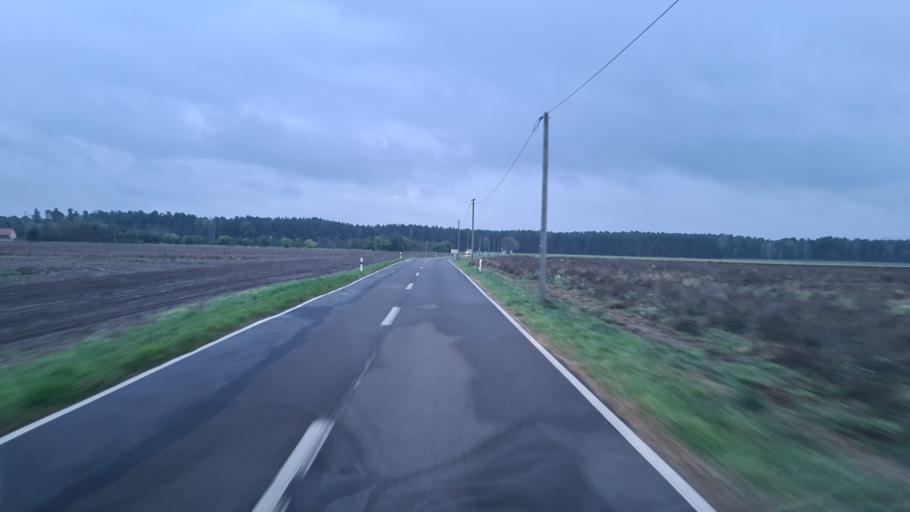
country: DE
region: Brandenburg
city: Schlepzig
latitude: 52.0122
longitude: 13.9335
